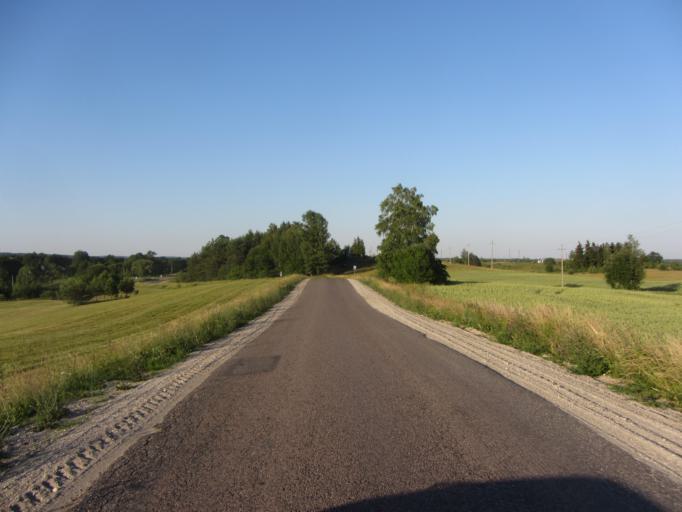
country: LT
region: Alytaus apskritis
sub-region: Alytus
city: Alytus
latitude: 54.2715
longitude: 24.1453
